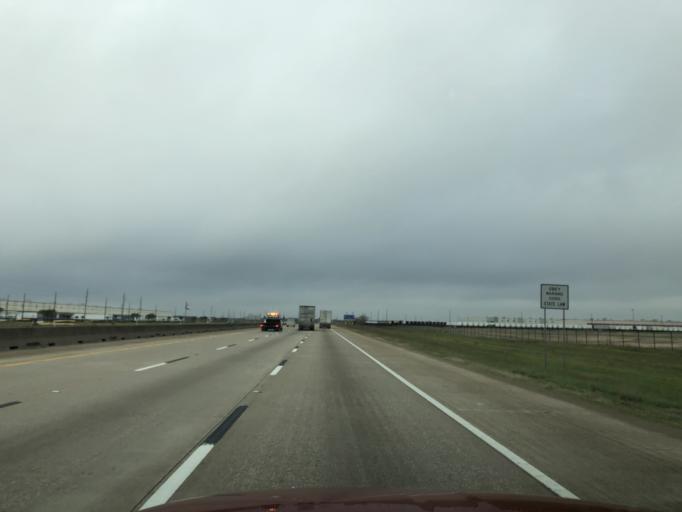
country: US
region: Texas
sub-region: Waller County
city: Brookshire
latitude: 29.7774
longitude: -95.9068
